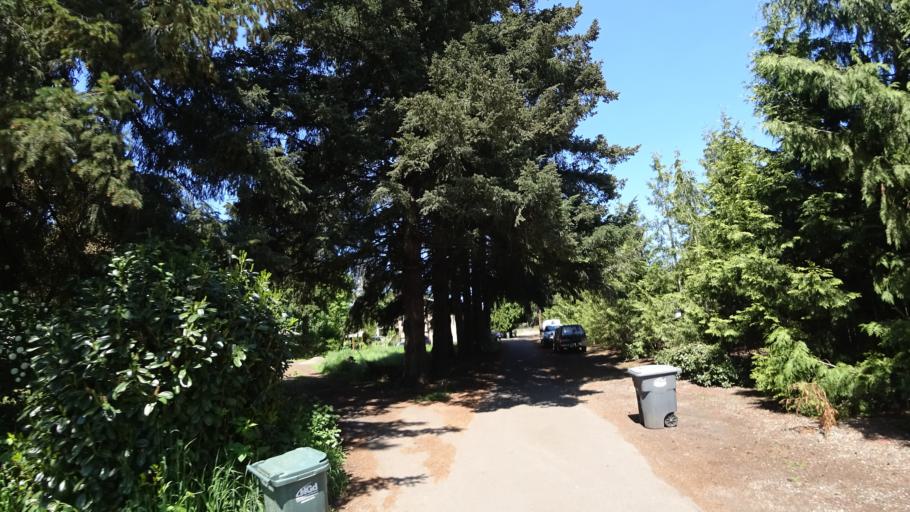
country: US
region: Oregon
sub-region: Washington County
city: Hillsboro
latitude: 45.5117
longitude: -122.9767
